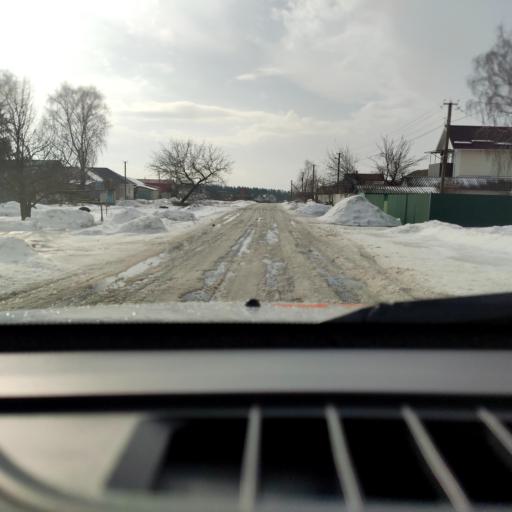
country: RU
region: Voronezj
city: Podgornoye
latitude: 51.7728
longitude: 39.1219
